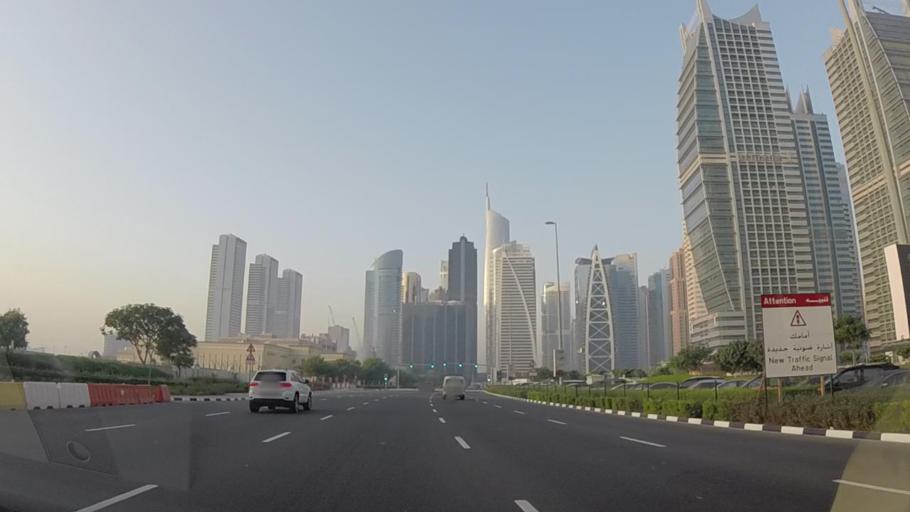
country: AE
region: Dubai
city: Dubai
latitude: 25.0758
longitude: 55.1477
